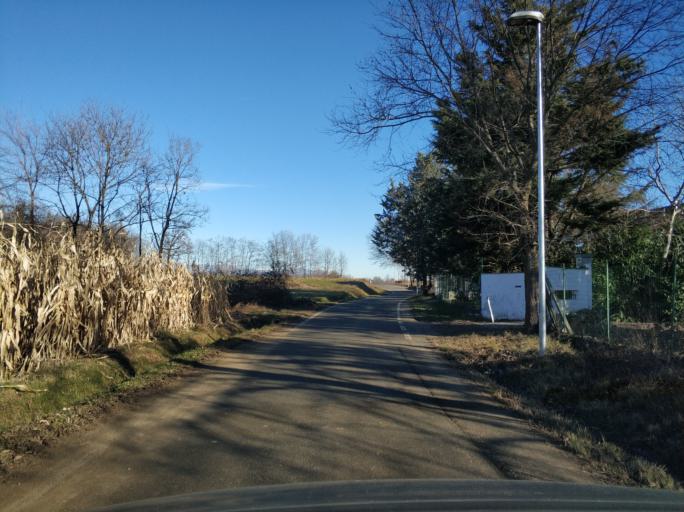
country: IT
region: Piedmont
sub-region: Provincia di Torino
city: San Francesco al Campo
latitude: 45.2378
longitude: 7.6434
